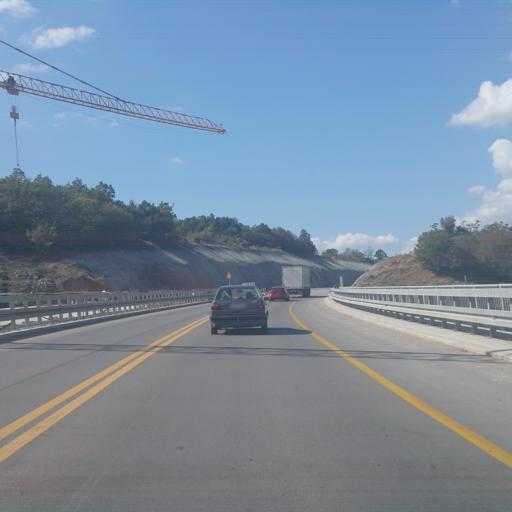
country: RS
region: Central Serbia
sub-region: Pirotski Okrug
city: Bela Palanka
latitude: 43.2192
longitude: 22.4123
